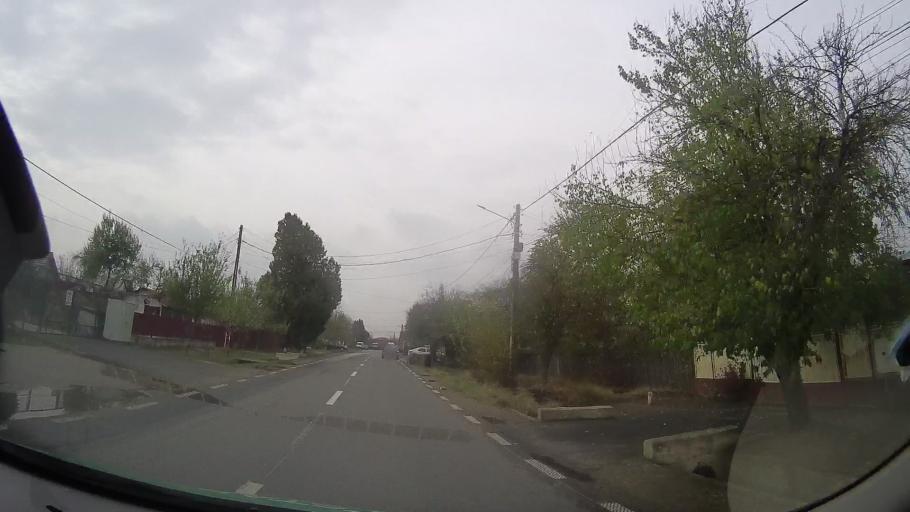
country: RO
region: Ilfov
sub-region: Comuna Gruiu
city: Gruiu
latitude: 44.7252
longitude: 26.2294
